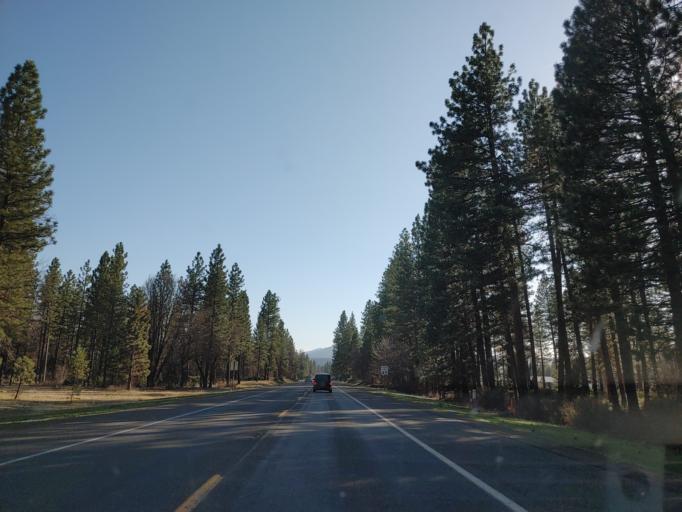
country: US
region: California
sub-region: Shasta County
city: Burney
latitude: 40.8966
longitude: -121.6468
